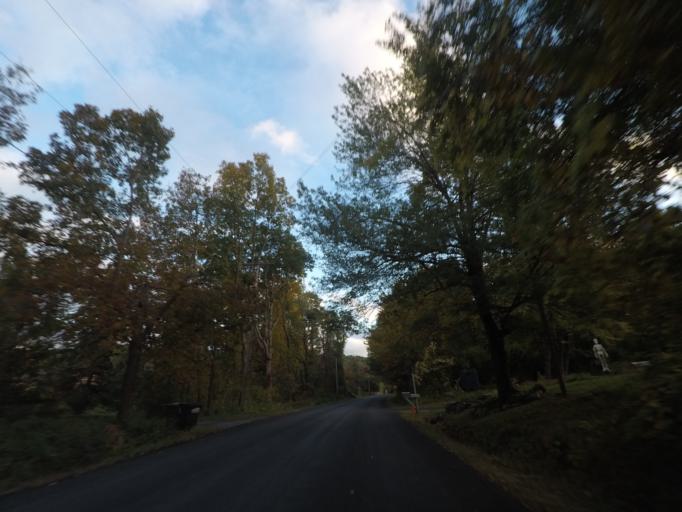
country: US
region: New York
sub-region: Rensselaer County
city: Nassau
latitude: 42.5201
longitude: -73.5903
